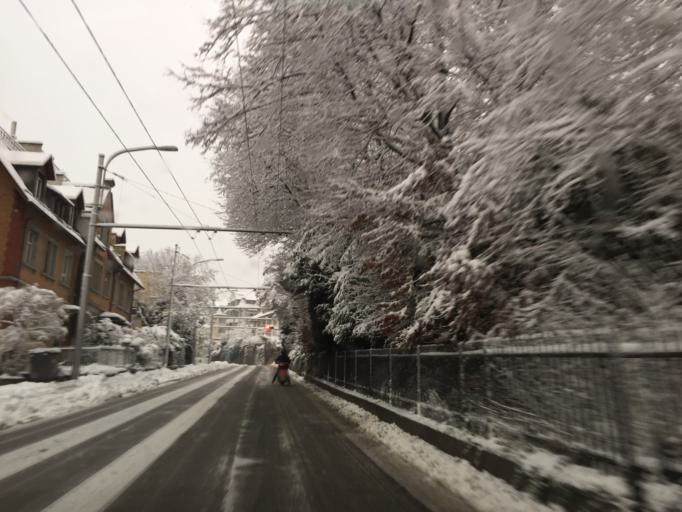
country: CH
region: Zurich
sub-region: Bezirk Zuerich
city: Zuerich (Kreis 7) / Hottingen
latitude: 47.3743
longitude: 8.5610
